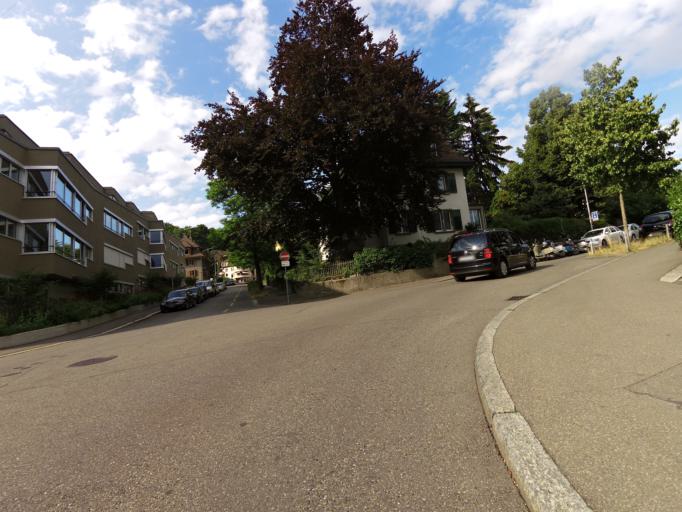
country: CH
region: Zurich
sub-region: Bezirk Zuerich
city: Zuerich (Kreis 10) / Wipkingen
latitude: 47.3956
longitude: 8.5300
